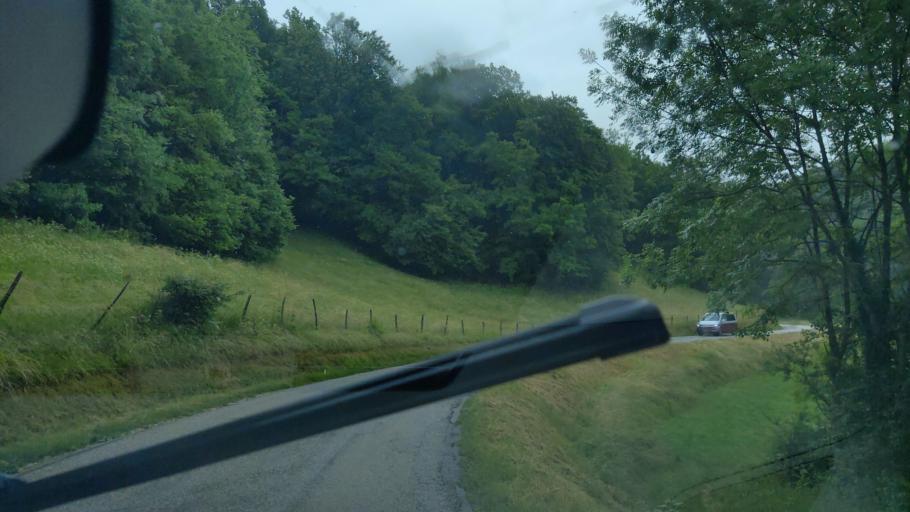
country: FR
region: Rhone-Alpes
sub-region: Departement de la Savoie
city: Chatillon
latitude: 45.7794
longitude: 5.8774
